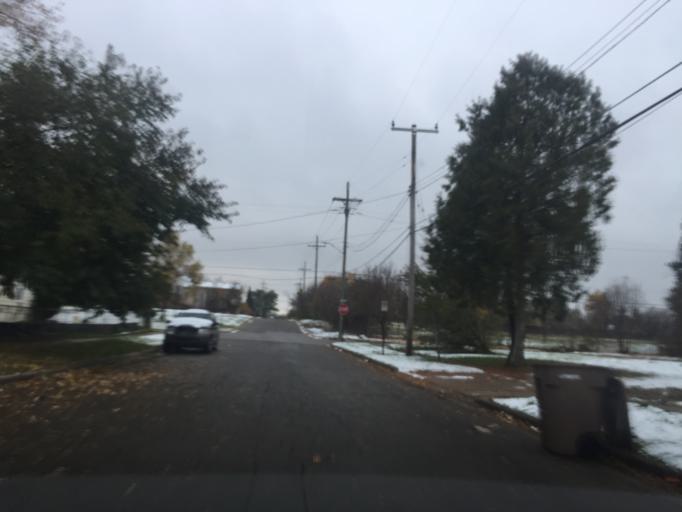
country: US
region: Michigan
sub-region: Oakland County
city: Pontiac
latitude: 42.6295
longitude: -83.2792
